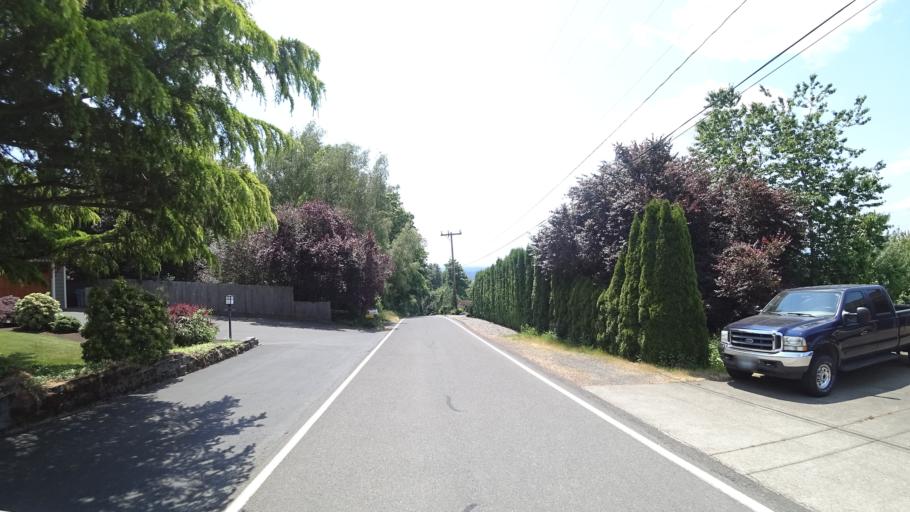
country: US
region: Oregon
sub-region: Clackamas County
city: Happy Valley
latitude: 45.4521
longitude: -122.5531
